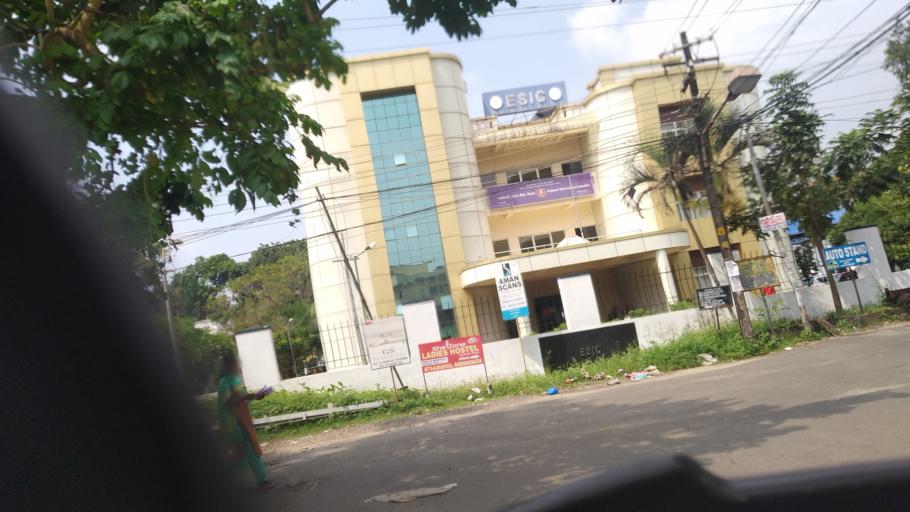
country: IN
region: Kerala
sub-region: Ernakulam
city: Cochin
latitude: 9.9934
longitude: 76.2855
